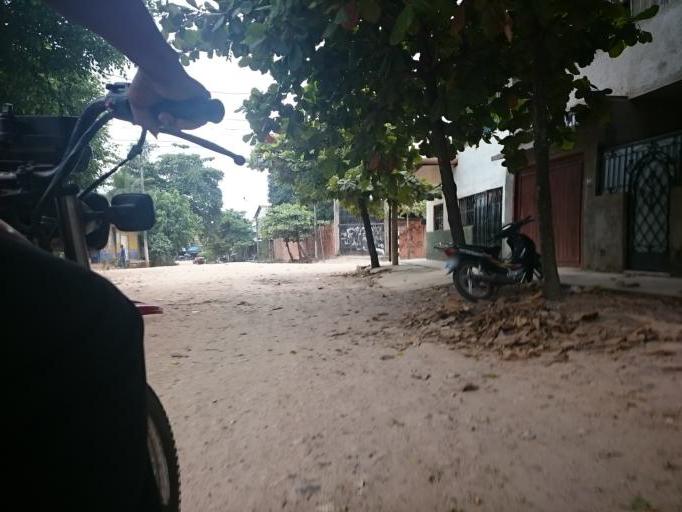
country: PE
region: Ucayali
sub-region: Provincia de Coronel Portillo
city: Pucallpa
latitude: -8.3788
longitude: -74.5403
